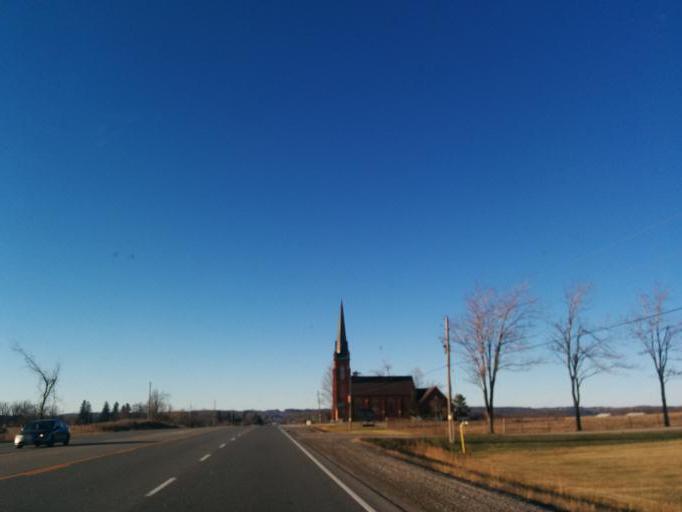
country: CA
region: Ontario
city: Brampton
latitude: 43.7955
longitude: -79.9081
